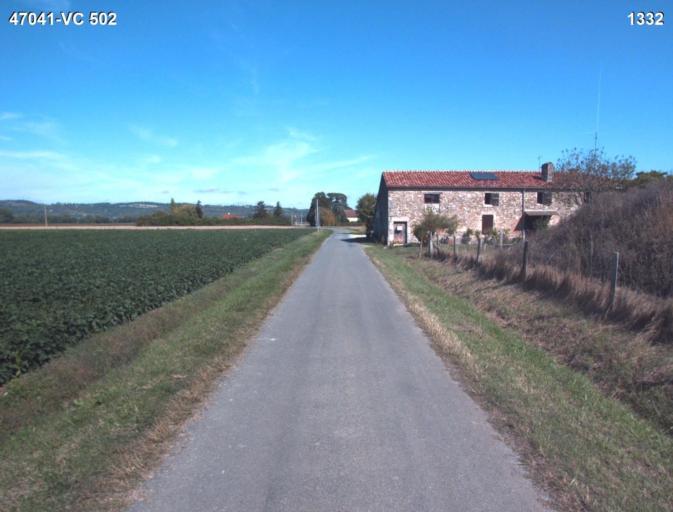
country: FR
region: Aquitaine
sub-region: Departement du Lot-et-Garonne
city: Port-Sainte-Marie
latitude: 44.2206
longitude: 0.3921
